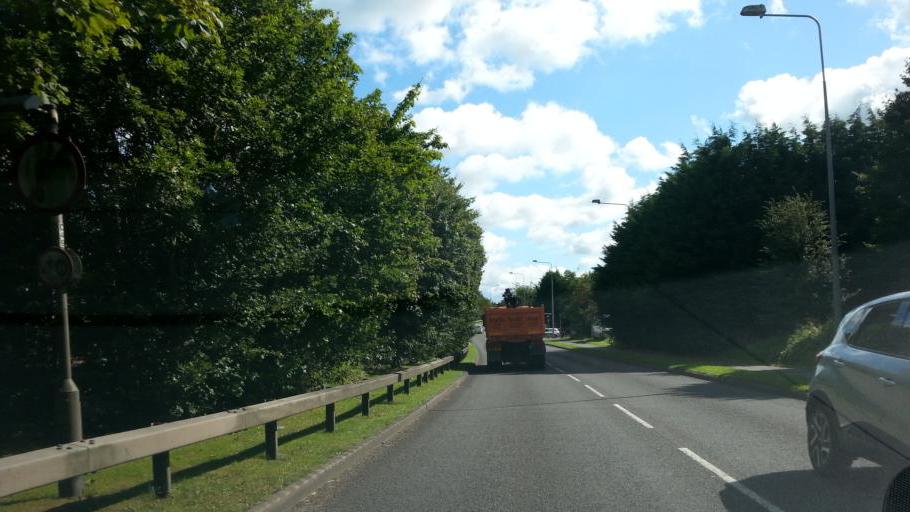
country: GB
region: England
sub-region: Staffordshire
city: Uttoxeter
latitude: 52.8948
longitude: -1.8660
